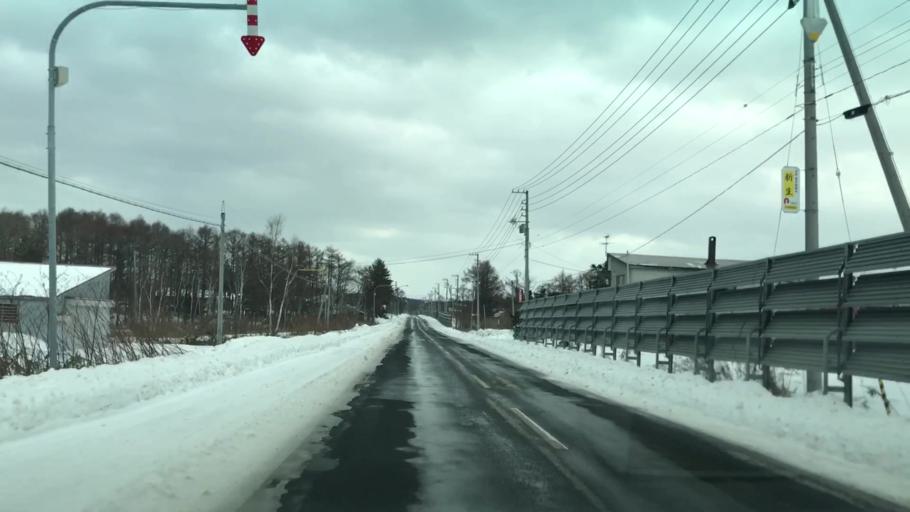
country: JP
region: Hokkaido
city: Yoichi
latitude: 43.3119
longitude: 140.5468
